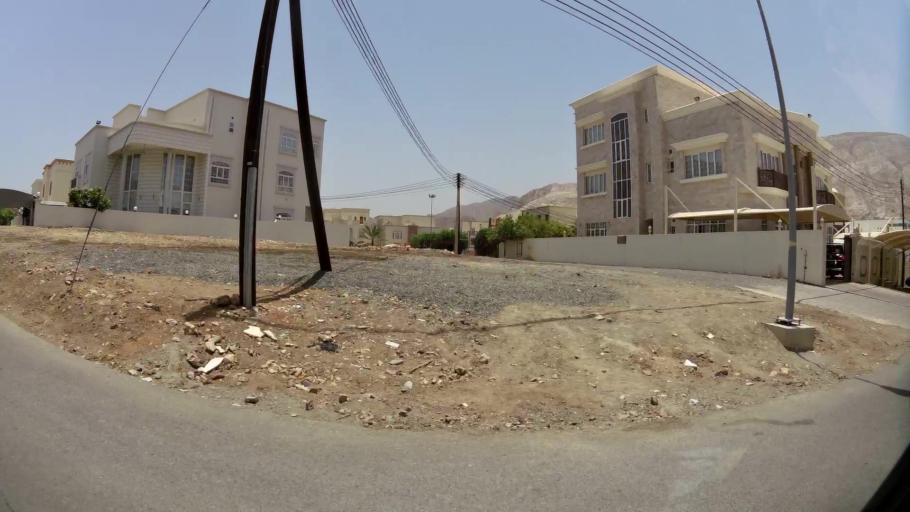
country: OM
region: Muhafazat Masqat
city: Bawshar
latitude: 23.5600
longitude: 58.4106
